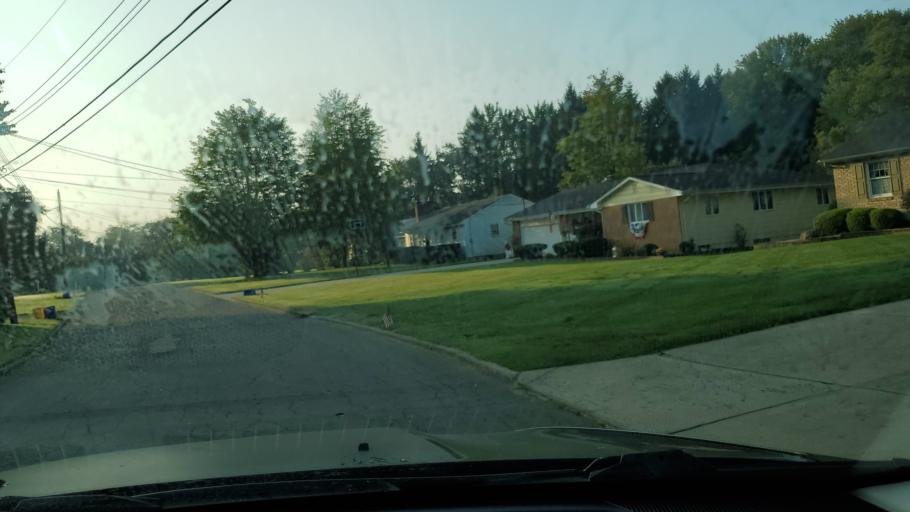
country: US
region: Ohio
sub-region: Mahoning County
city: Poland
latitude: 41.0297
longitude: -80.6125
